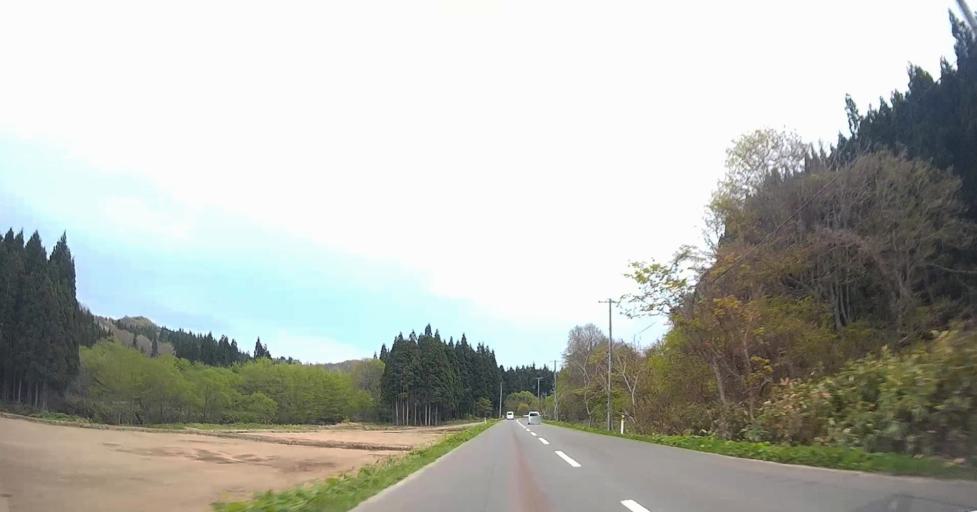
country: JP
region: Aomori
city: Goshogawara
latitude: 41.1221
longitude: 140.5222
